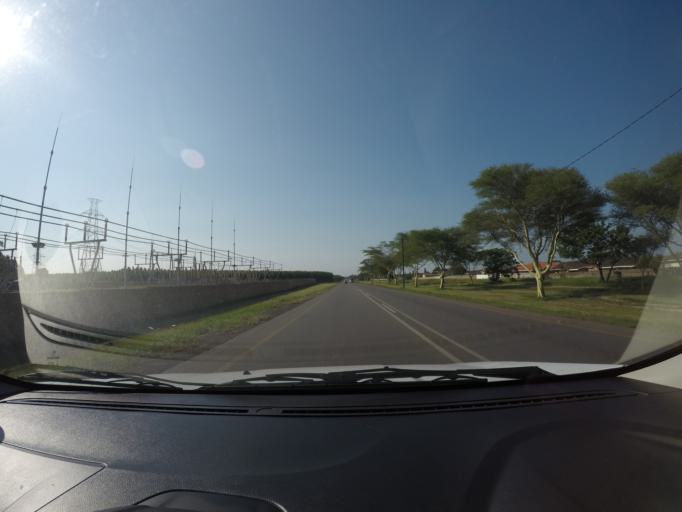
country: ZA
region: KwaZulu-Natal
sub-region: uThungulu District Municipality
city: Richards Bay
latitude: -28.7243
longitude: 32.0349
